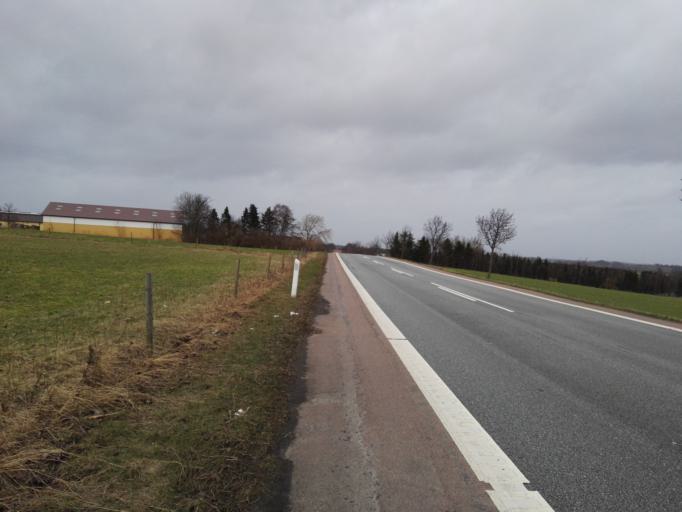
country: DK
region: Capital Region
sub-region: Frederikssund Kommune
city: Skibby
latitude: 55.6781
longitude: 11.9295
